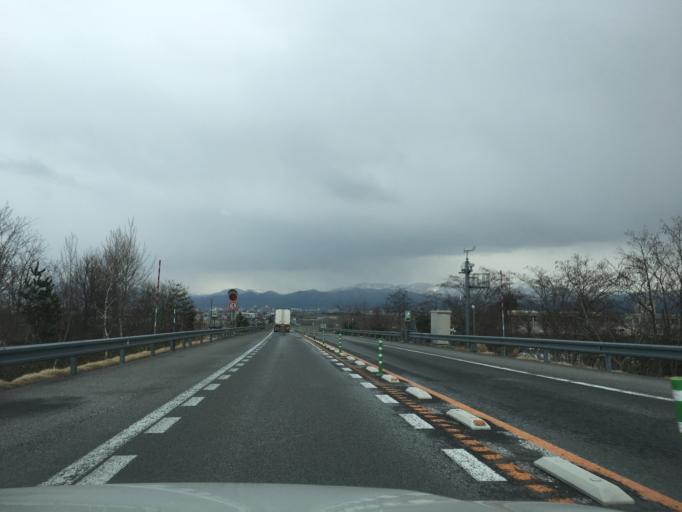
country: JP
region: Aomori
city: Aomori Shi
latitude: 40.7975
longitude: 140.7079
